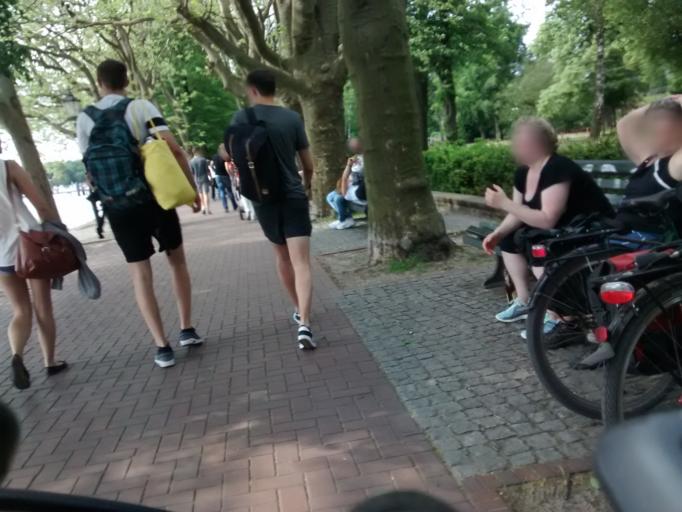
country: DE
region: Berlin
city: Tegel
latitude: 52.5856
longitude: 13.2752
